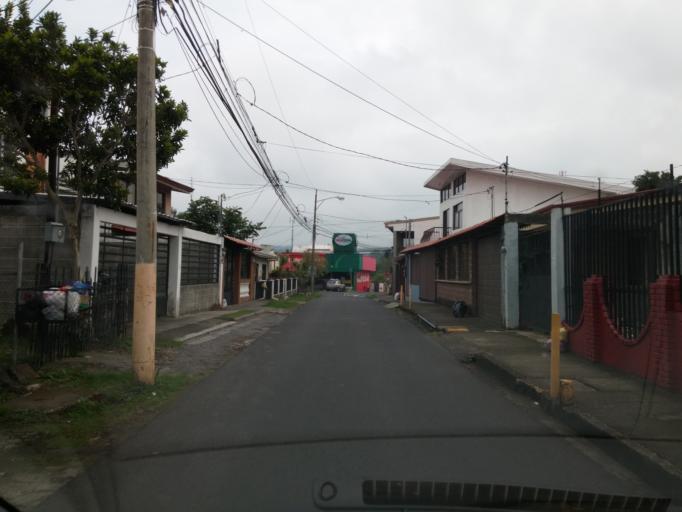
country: CR
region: Heredia
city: Llorente
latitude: 10.0154
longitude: -84.1511
